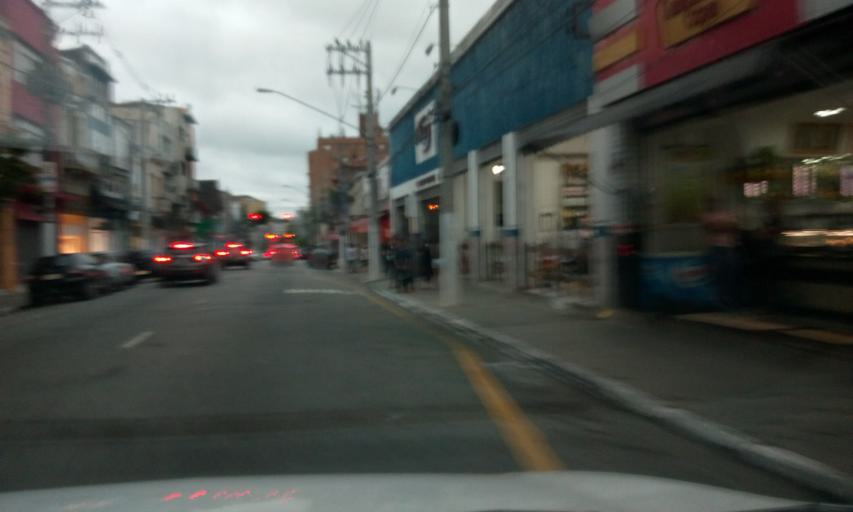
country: BR
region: Sao Paulo
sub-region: Sao Paulo
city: Sao Paulo
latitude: -23.5350
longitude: -46.6300
